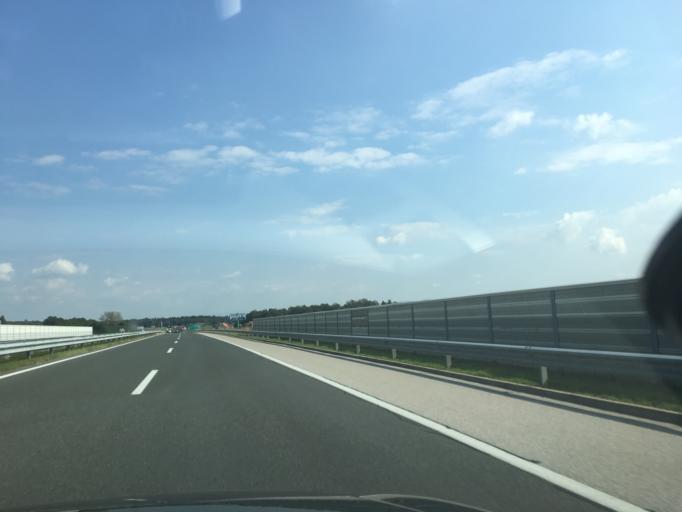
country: SI
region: Kostanjevica na Krki
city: Kostanjevica na Krki
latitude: 45.9072
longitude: 15.3832
